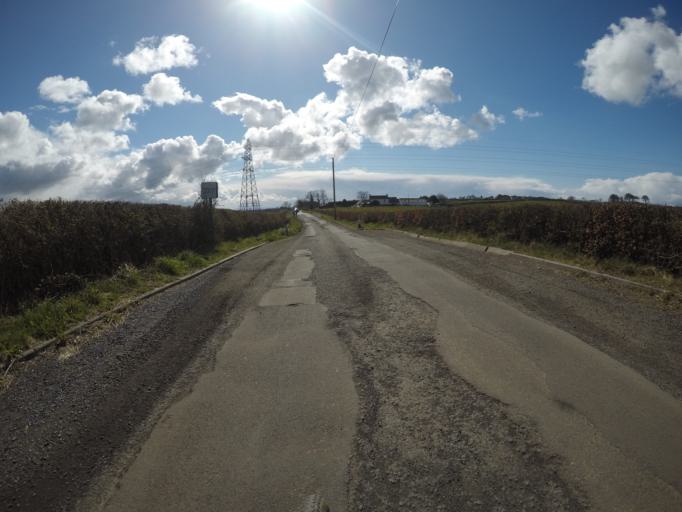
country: GB
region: Scotland
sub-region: North Ayrshire
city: Kilwinning
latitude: 55.6729
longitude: -4.7223
